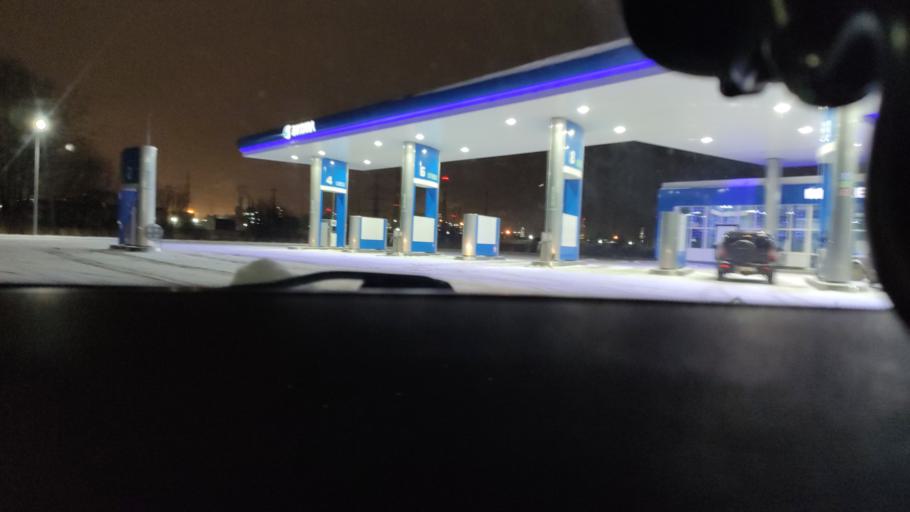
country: RU
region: Perm
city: Kondratovo
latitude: 57.9330
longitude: 56.1238
